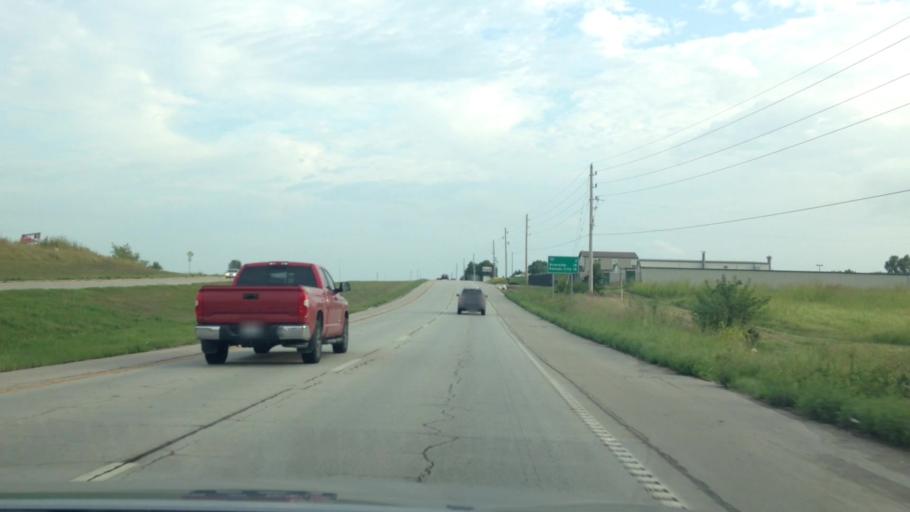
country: US
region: Missouri
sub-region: Clay County
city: Smithville
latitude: 39.3587
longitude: -94.5840
